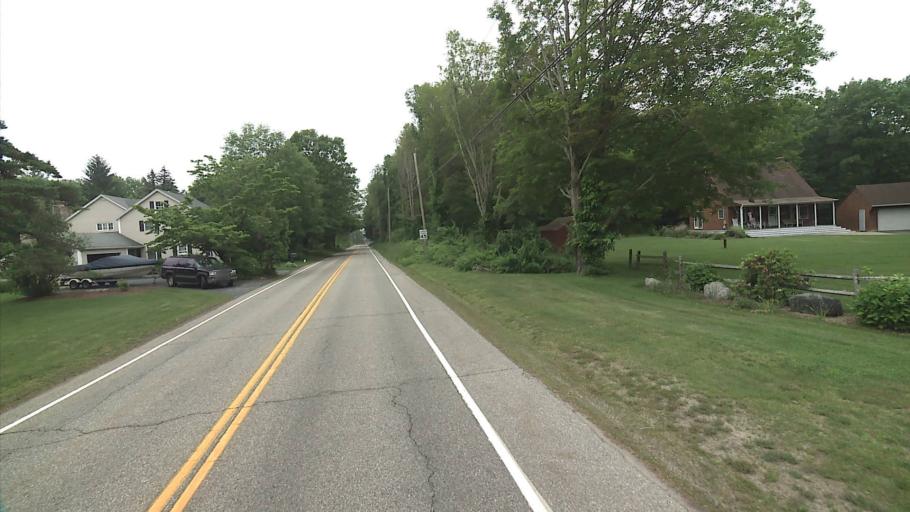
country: US
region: Connecticut
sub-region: Tolland County
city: Hebron
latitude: 41.7203
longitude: -72.3718
